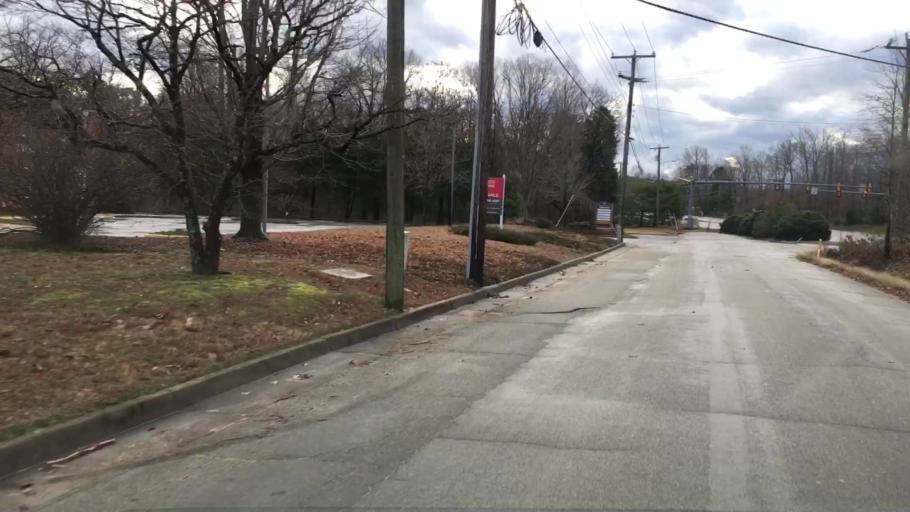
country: US
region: Virginia
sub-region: Chesterfield County
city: Bon Air
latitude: 37.4976
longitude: -77.6062
